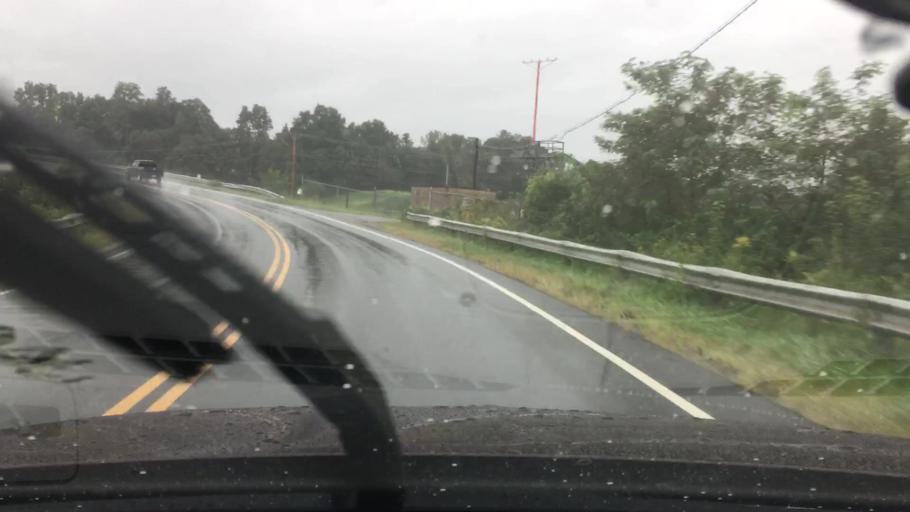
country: US
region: New York
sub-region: Dutchess County
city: Myers Corner
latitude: 41.6218
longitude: -73.8929
